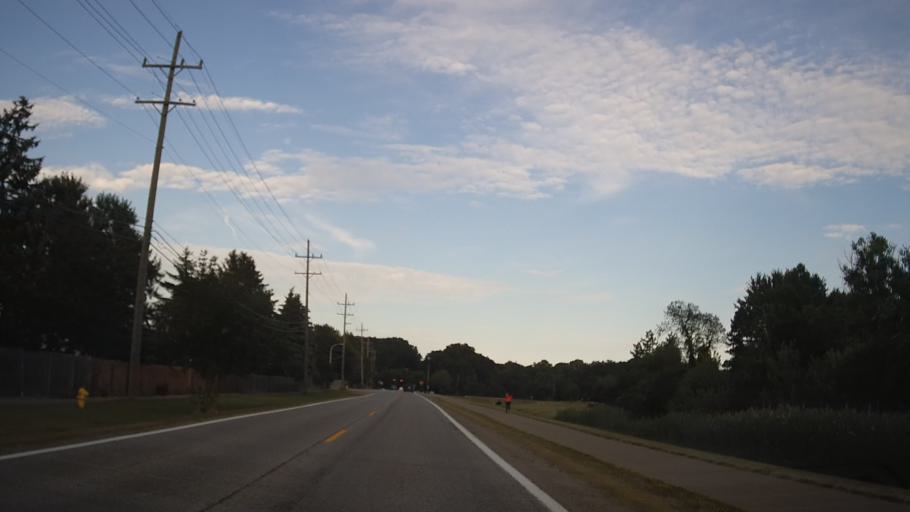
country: US
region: Michigan
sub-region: Macomb County
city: Clinton
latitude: 42.5975
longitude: -82.9213
